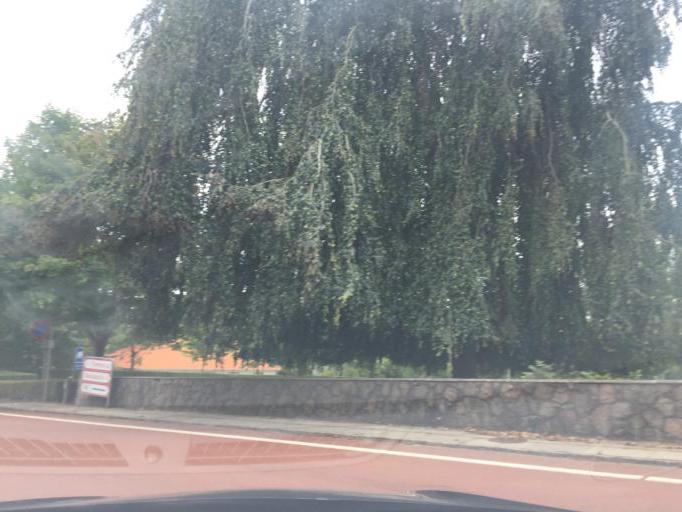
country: DK
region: South Denmark
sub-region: Assens Kommune
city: Tommerup Stationsby
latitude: 55.3542
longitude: 10.1851
